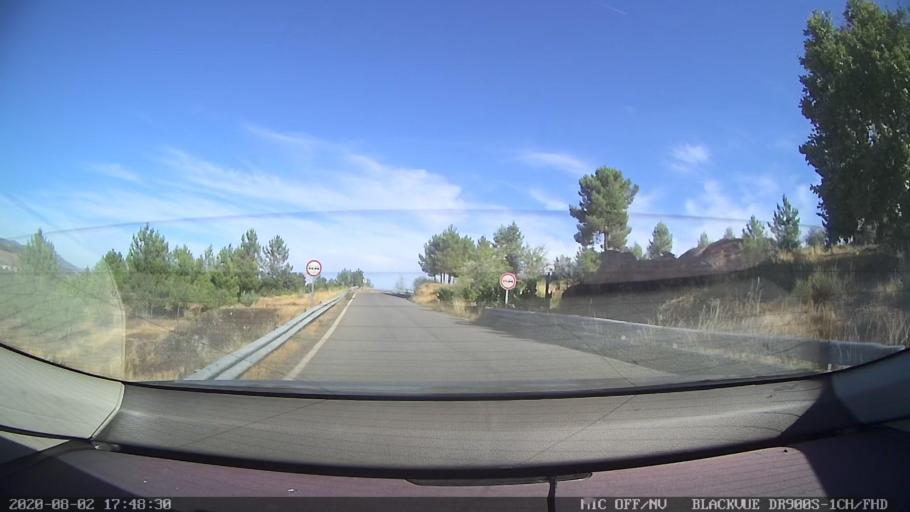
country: PT
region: Vila Real
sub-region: Murca
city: Murca
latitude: 41.4029
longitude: -7.4767
